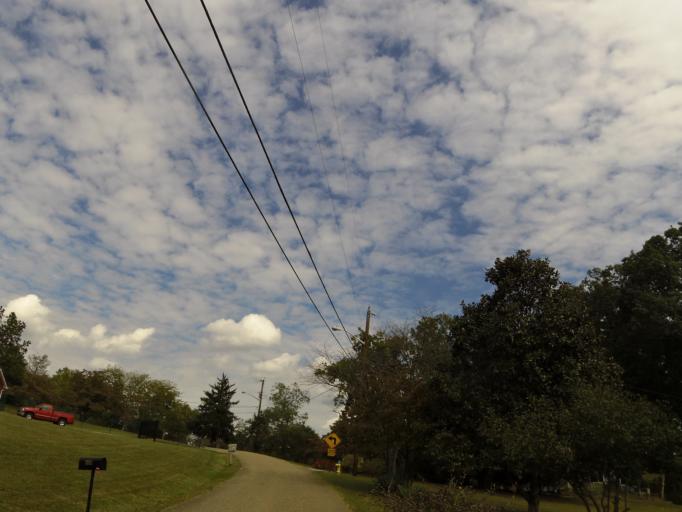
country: US
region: Tennessee
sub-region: Knox County
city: Mascot
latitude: 36.0006
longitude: -83.8265
